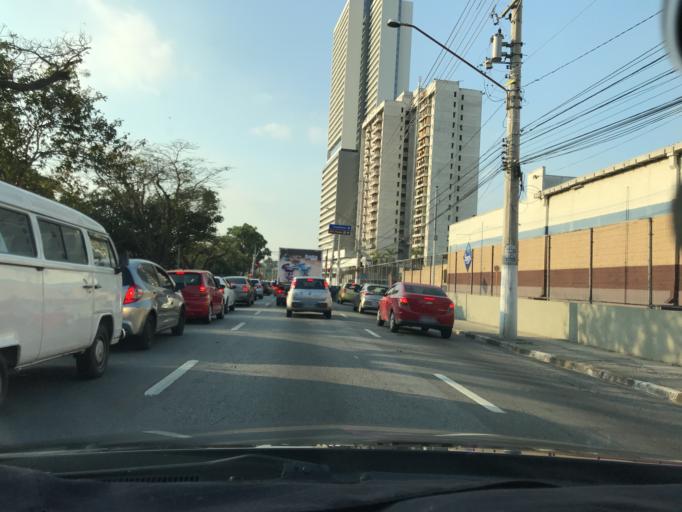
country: BR
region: Sao Paulo
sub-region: Osasco
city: Osasco
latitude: -23.5343
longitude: -46.7728
